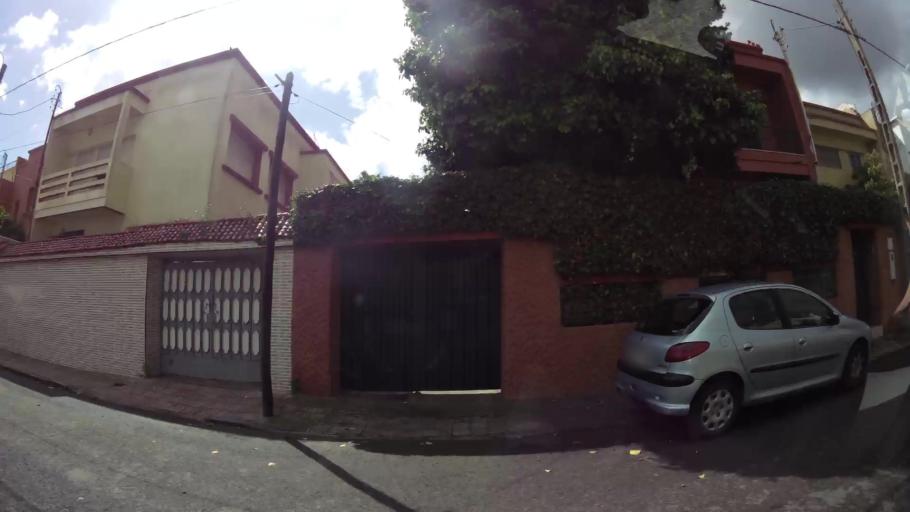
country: MA
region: Grand Casablanca
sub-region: Casablanca
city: Casablanca
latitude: 33.5535
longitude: -7.6087
